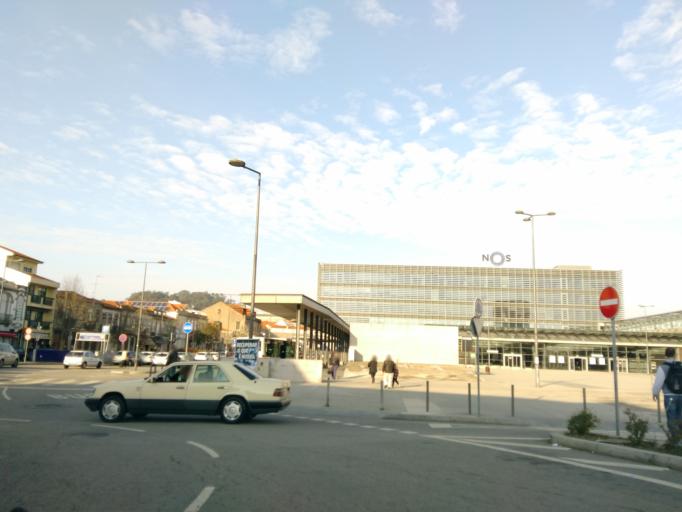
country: PT
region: Porto
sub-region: Vila Nova de Gaia
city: Oliveira do Douro
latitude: 41.1488
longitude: -8.5860
